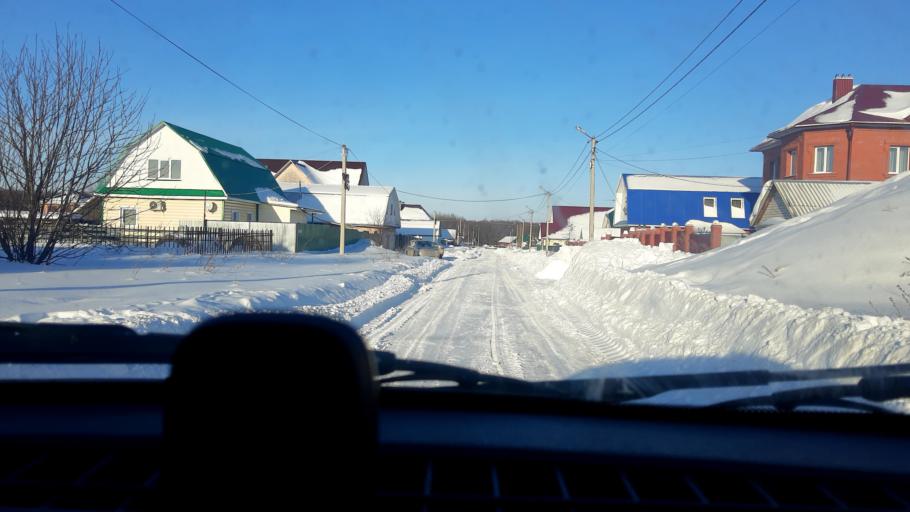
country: RU
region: Bashkortostan
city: Kabakovo
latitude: 54.6214
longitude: 56.0853
